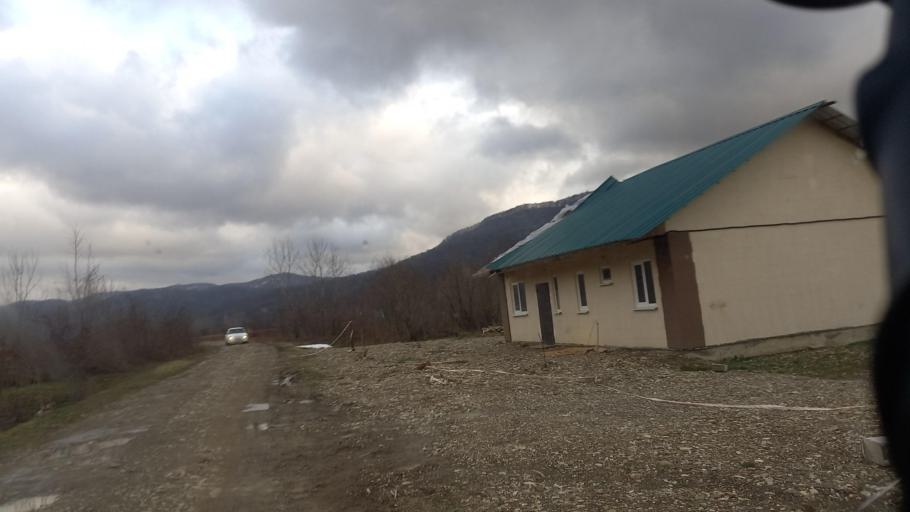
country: RU
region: Krasnodarskiy
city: Lermontovo
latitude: 44.4318
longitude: 38.7958
